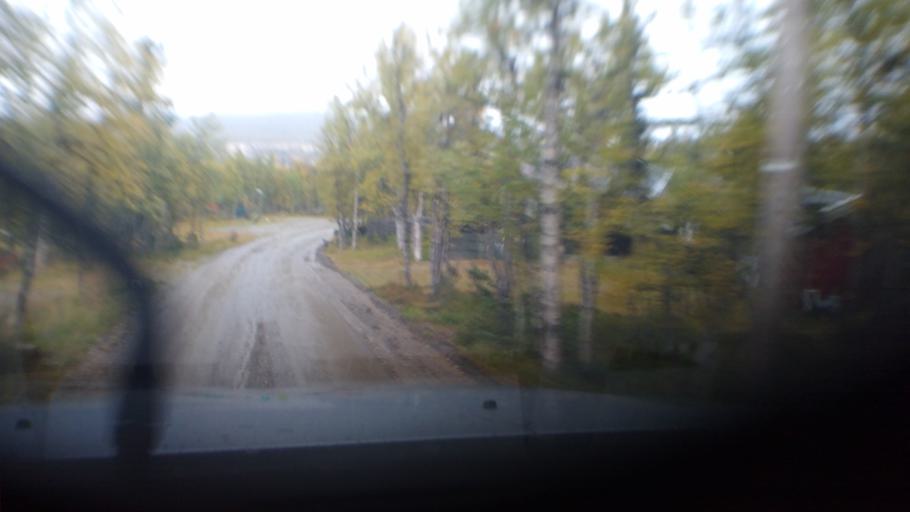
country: NO
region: Oppland
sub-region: Ringebu
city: Ringebu
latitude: 61.6518
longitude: 10.0991
